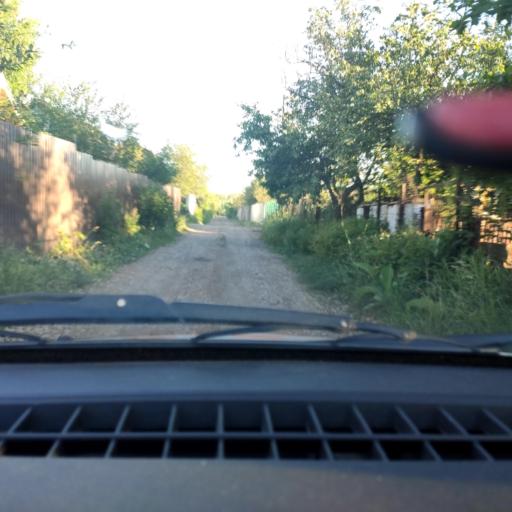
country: RU
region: Bashkortostan
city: Karmaskaly
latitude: 54.3701
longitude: 55.9033
